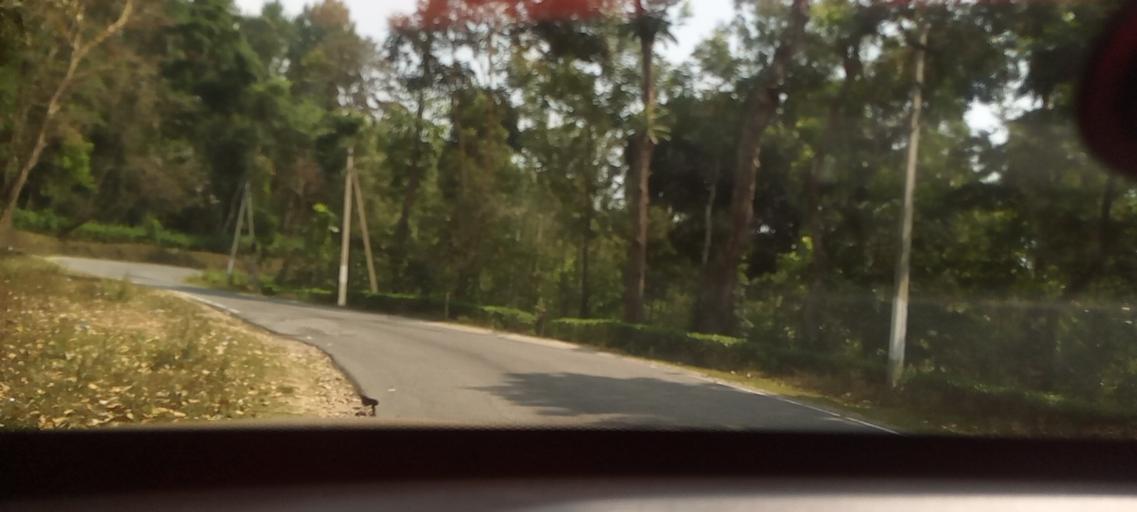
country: IN
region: Karnataka
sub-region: Chikmagalur
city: Mudigere
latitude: 13.2574
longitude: 75.6338
